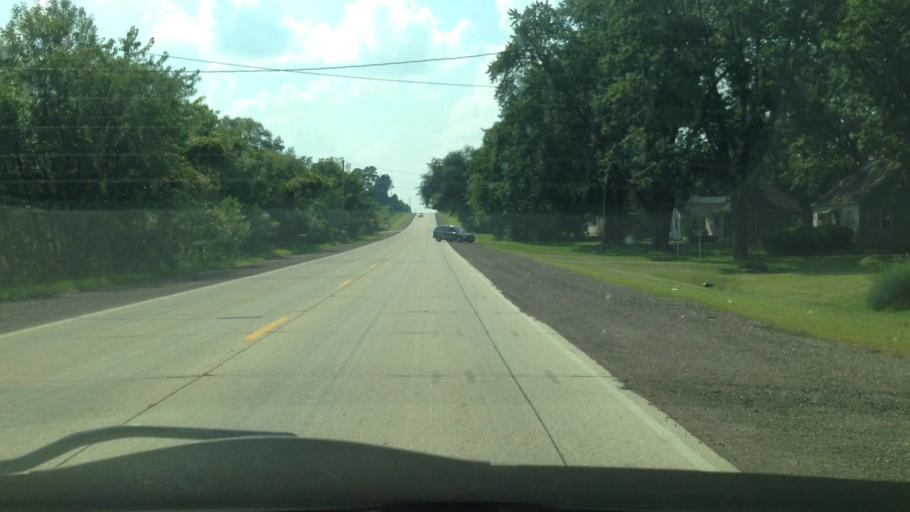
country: US
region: Iowa
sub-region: Black Hawk County
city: Waterloo
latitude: 42.5422
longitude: -92.3400
